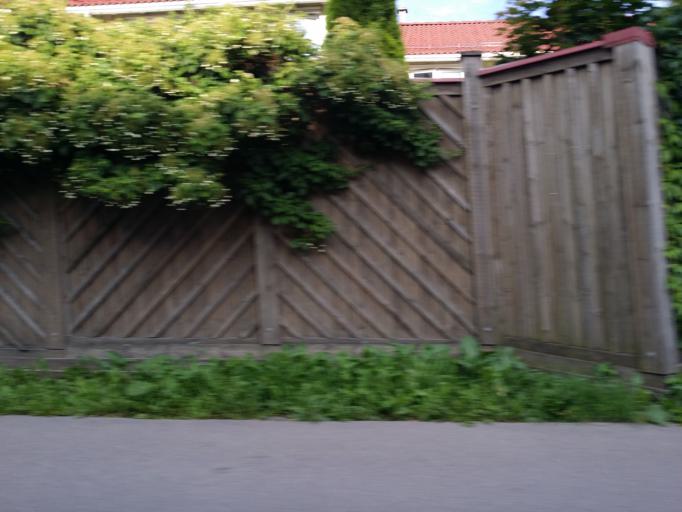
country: NO
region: Akershus
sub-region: Oppegard
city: Kolbotn
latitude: 59.9006
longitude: 10.8516
